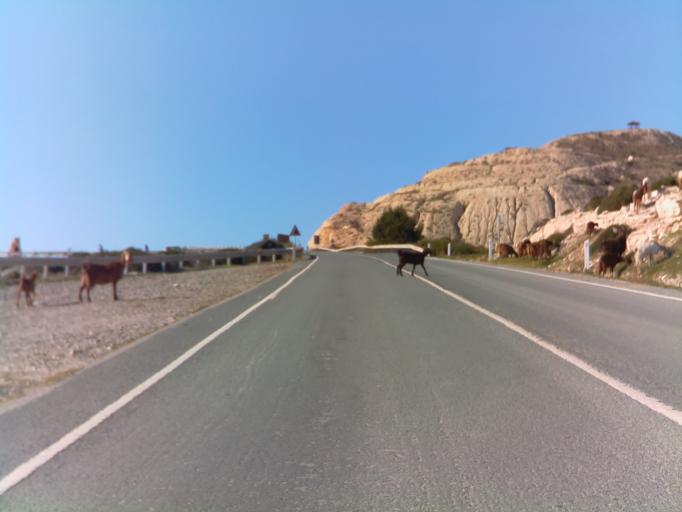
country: CY
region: Limassol
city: Pissouri
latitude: 34.6602
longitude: 32.6438
